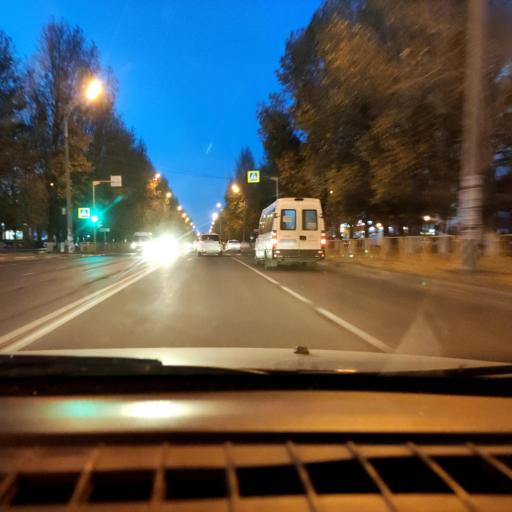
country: RU
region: Samara
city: Tol'yatti
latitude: 53.5365
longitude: 49.3444
